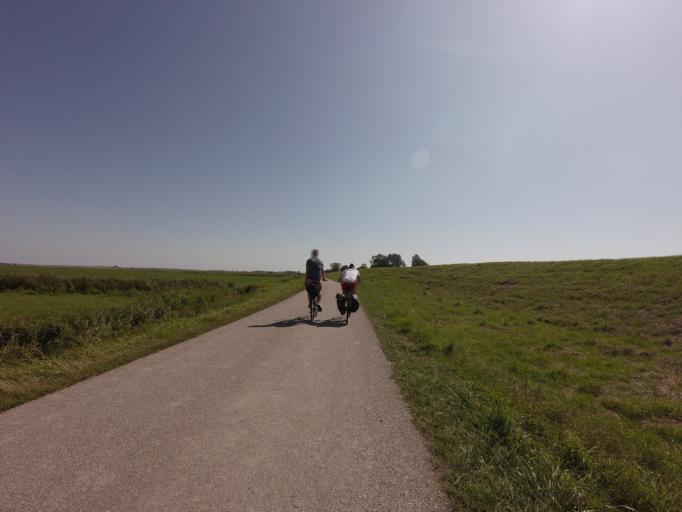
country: NL
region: Friesland
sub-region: Gemeente Dongeradeel
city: Anjum
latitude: 53.3941
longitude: 6.1123
